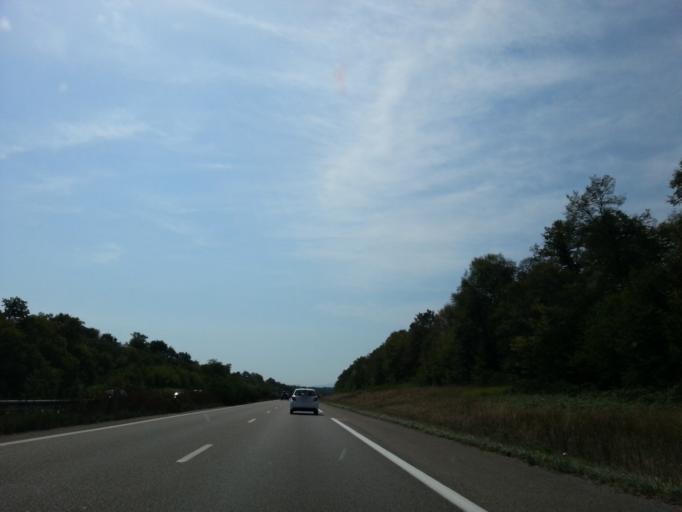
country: FR
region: Alsace
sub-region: Departement du Haut-Rhin
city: Bartenheim
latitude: 47.6608
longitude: 7.4835
